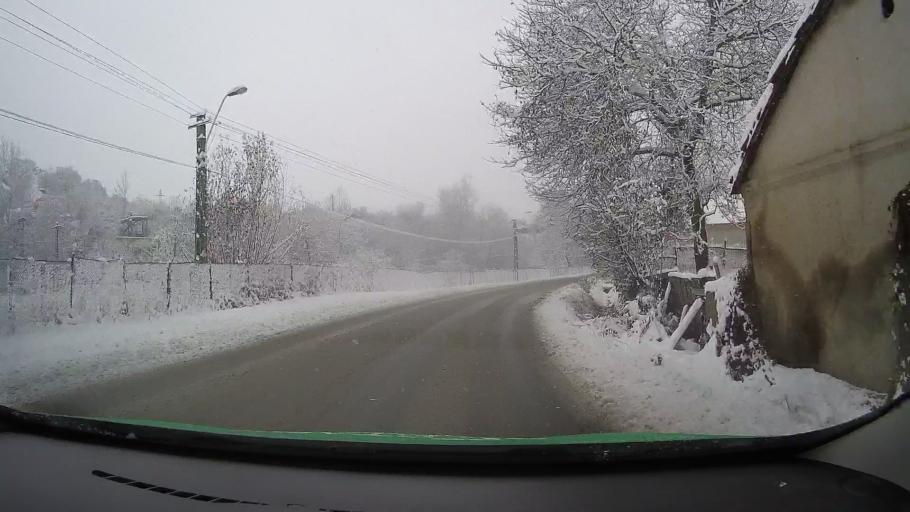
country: RO
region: Hunedoara
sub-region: Comuna Teliucu Inferior
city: Teliucu Inferior
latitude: 45.7356
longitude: 22.8833
